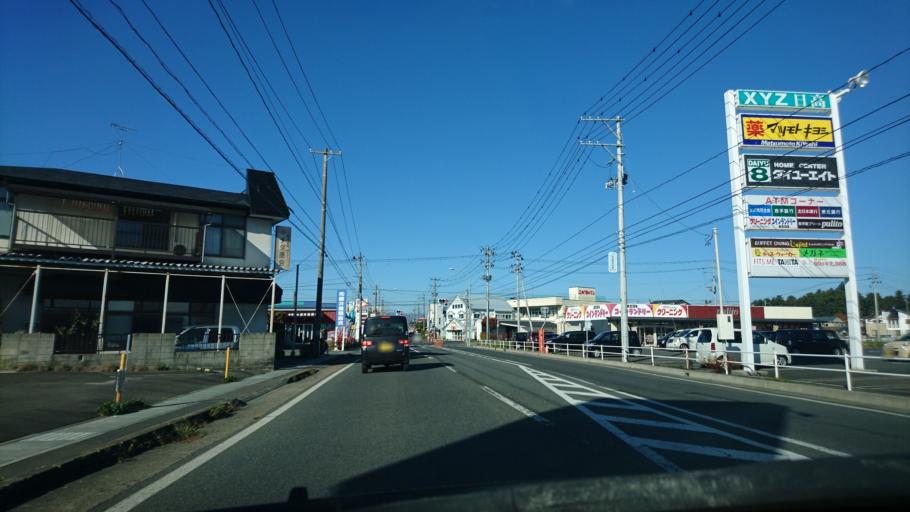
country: JP
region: Iwate
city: Mizusawa
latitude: 39.1392
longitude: 141.1343
